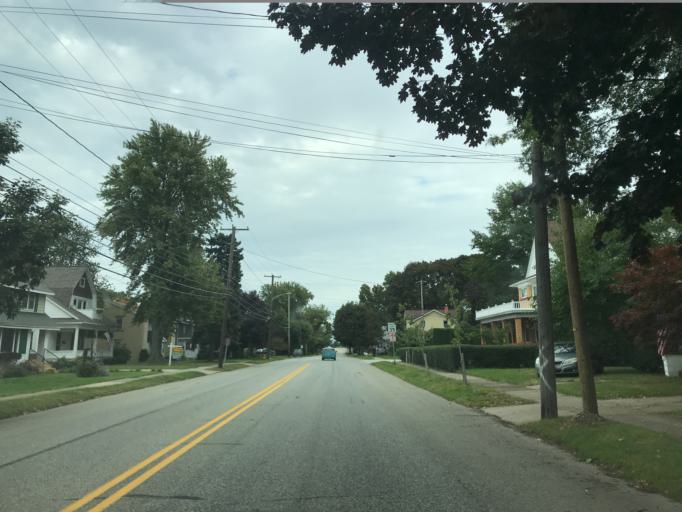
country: US
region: Pennsylvania
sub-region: Erie County
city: North East
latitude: 42.2181
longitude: -79.8272
